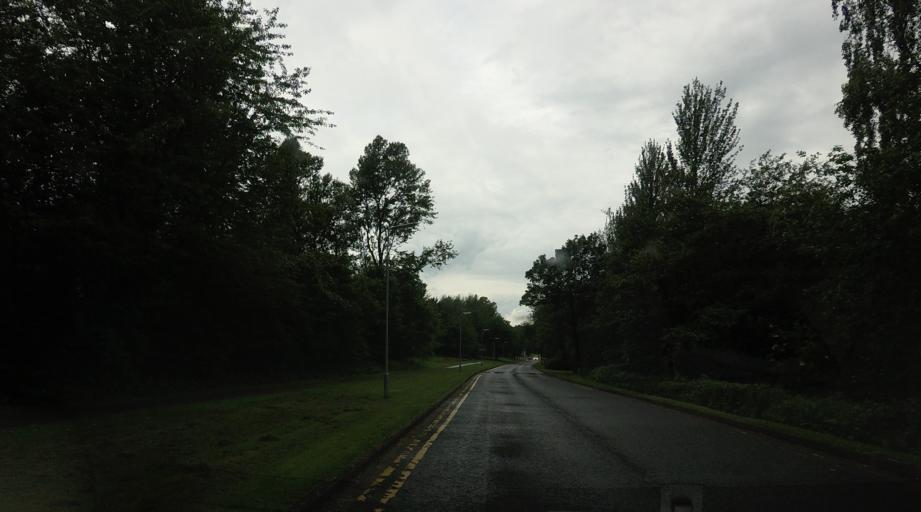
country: GB
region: Scotland
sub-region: Fife
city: Ballingry
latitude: 56.1493
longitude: -3.3311
